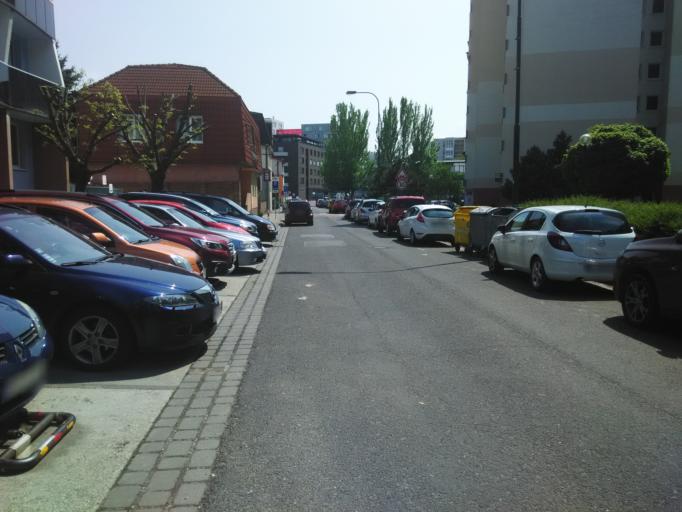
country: SK
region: Bratislavsky
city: Bratislava
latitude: 48.1576
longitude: 17.1401
